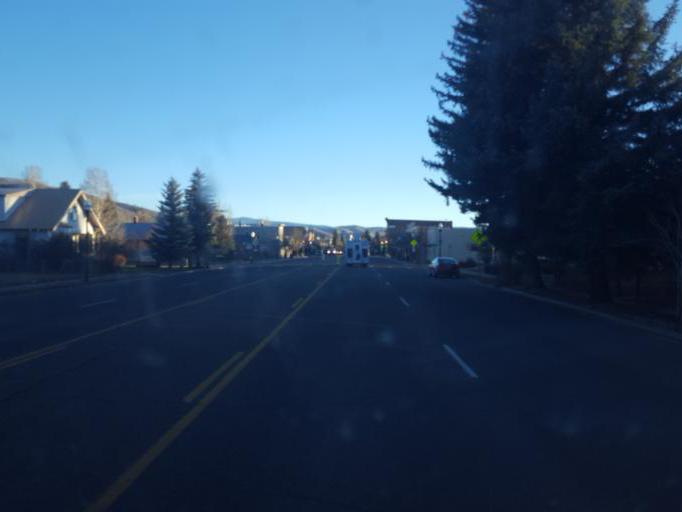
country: US
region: Colorado
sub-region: Gunnison County
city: Gunnison
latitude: 38.5488
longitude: -106.9270
